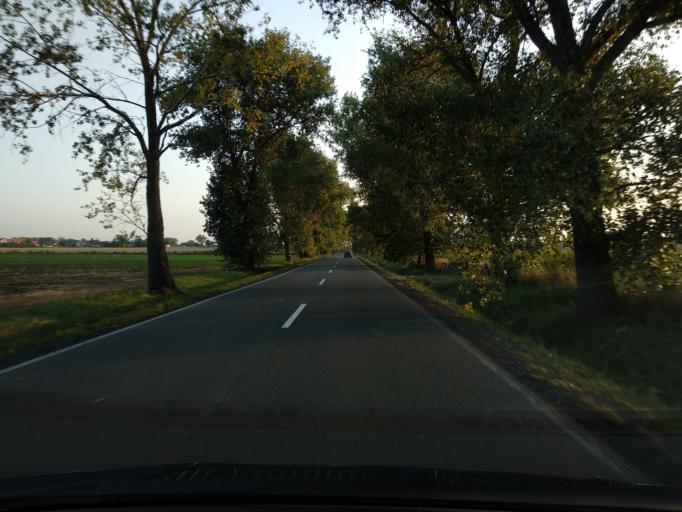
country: PL
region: Lower Silesian Voivodeship
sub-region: Powiat strzelinski
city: Strzelin
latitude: 50.8366
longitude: 17.0562
